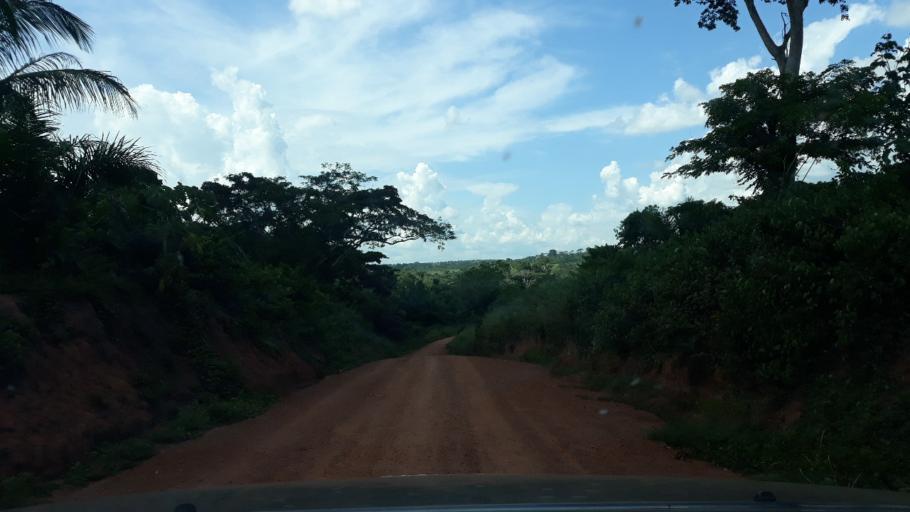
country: CD
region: Equateur
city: Businga
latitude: 3.4025
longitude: 20.3810
